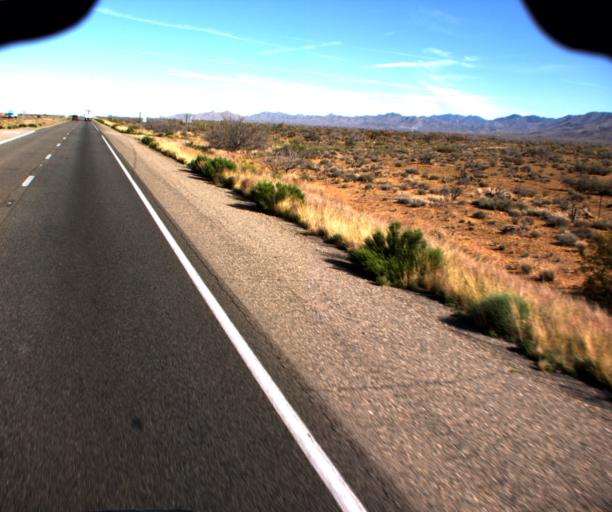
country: US
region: Arizona
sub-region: Mohave County
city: Golden Valley
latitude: 35.3088
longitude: -114.1954
